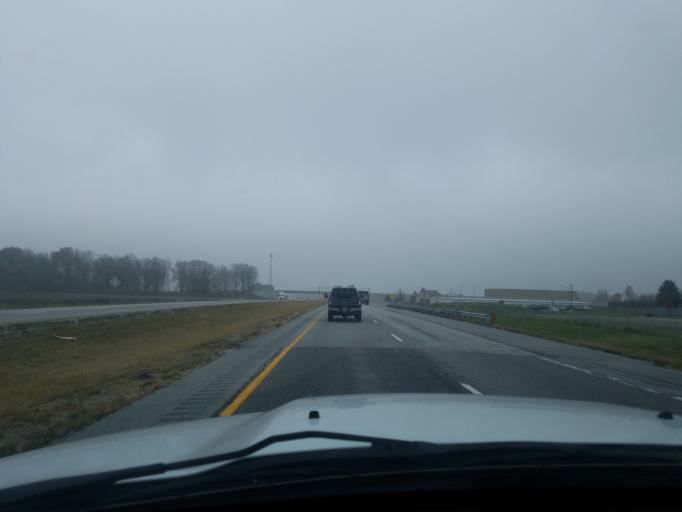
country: US
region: Indiana
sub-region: Howard County
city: Indian Heights
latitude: 40.3857
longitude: -86.1271
